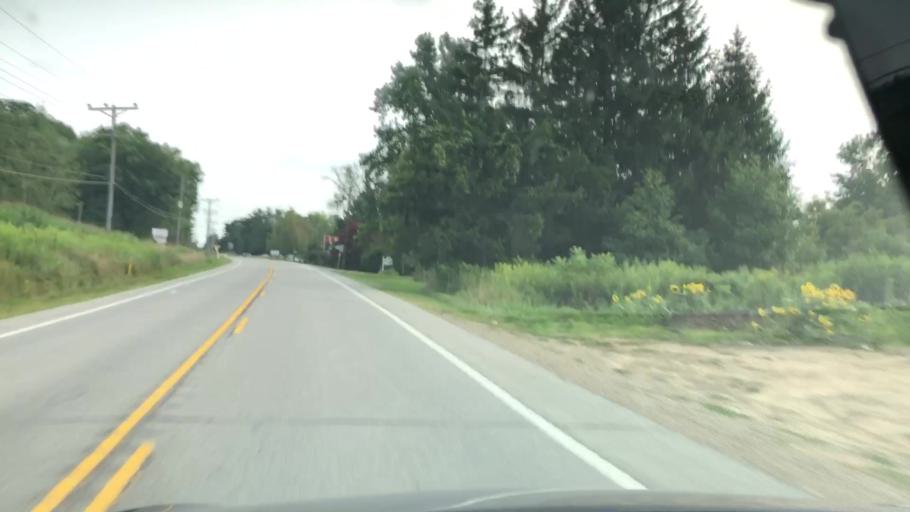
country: US
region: Pennsylvania
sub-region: Crawford County
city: Titusville
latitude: 41.5927
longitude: -79.6831
